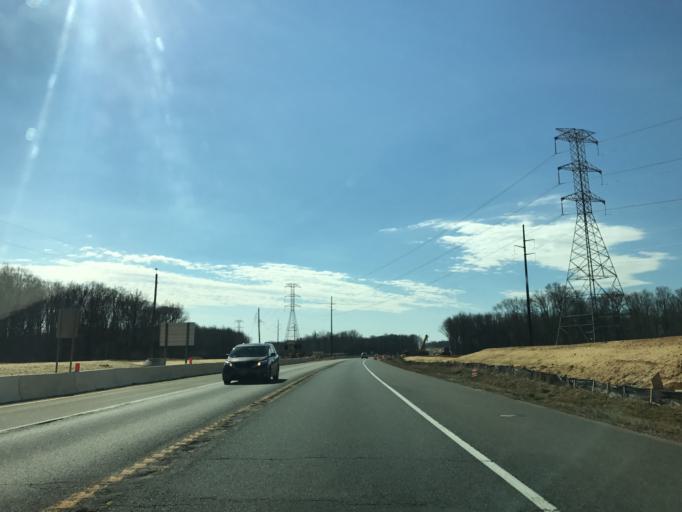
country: US
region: Delaware
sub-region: New Castle County
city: Middletown
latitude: 39.4178
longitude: -75.7650
